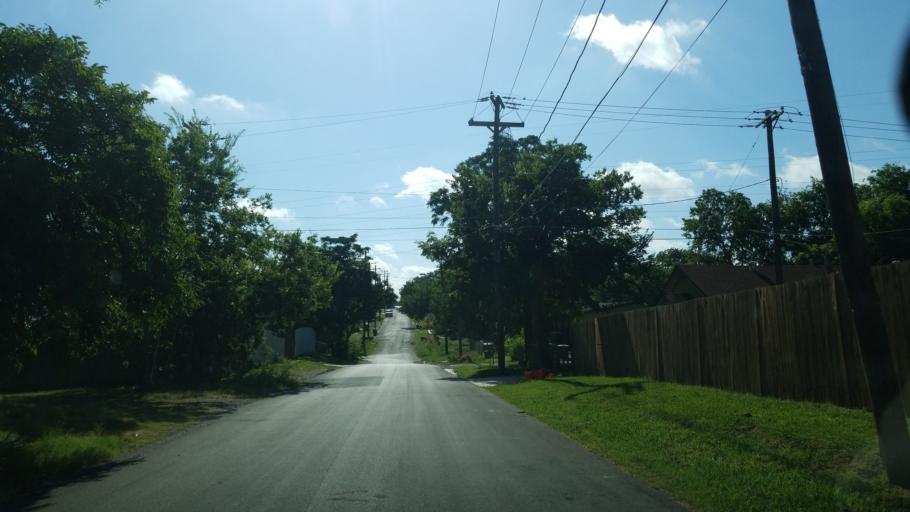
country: US
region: Texas
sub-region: Dallas County
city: Dallas
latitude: 32.7191
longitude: -96.8095
